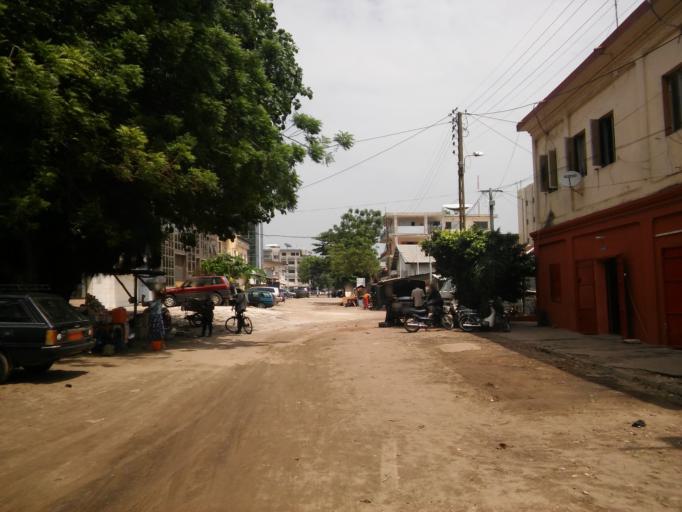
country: BJ
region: Littoral
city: Cotonou
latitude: 6.3610
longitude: 2.4328
